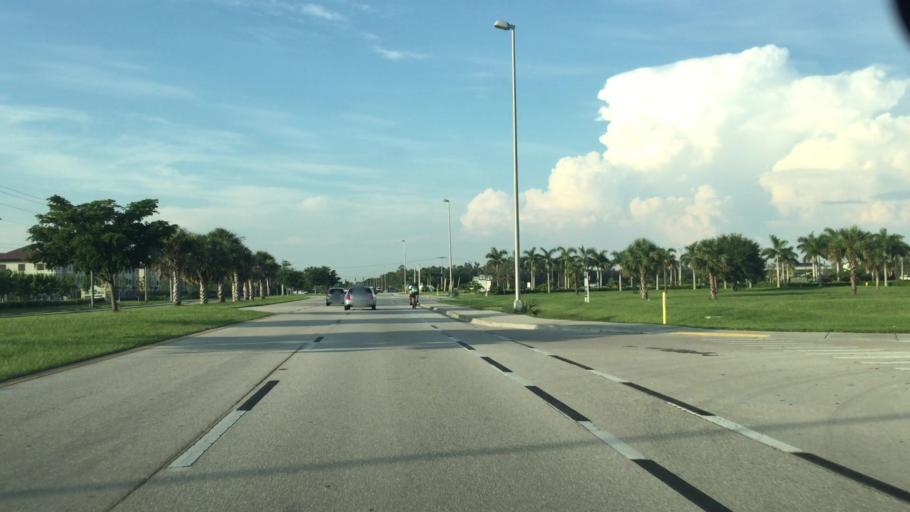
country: US
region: Florida
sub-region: Lee County
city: Three Oaks
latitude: 26.4529
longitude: -81.7889
